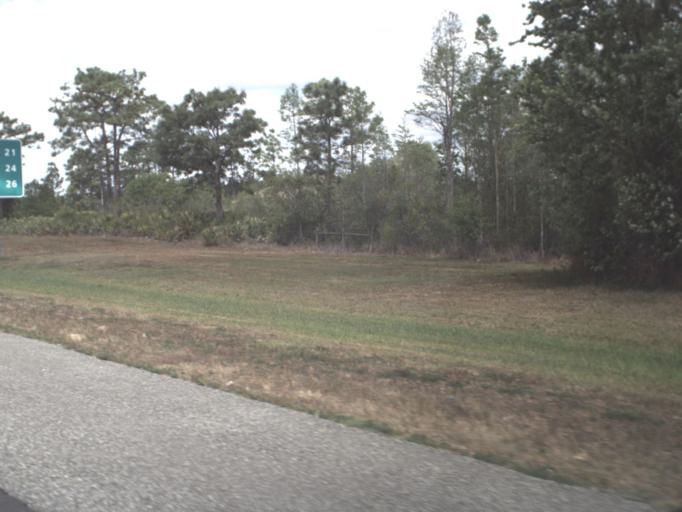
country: US
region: Florida
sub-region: Orange County
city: Wedgefield
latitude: 28.4519
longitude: -81.0801
